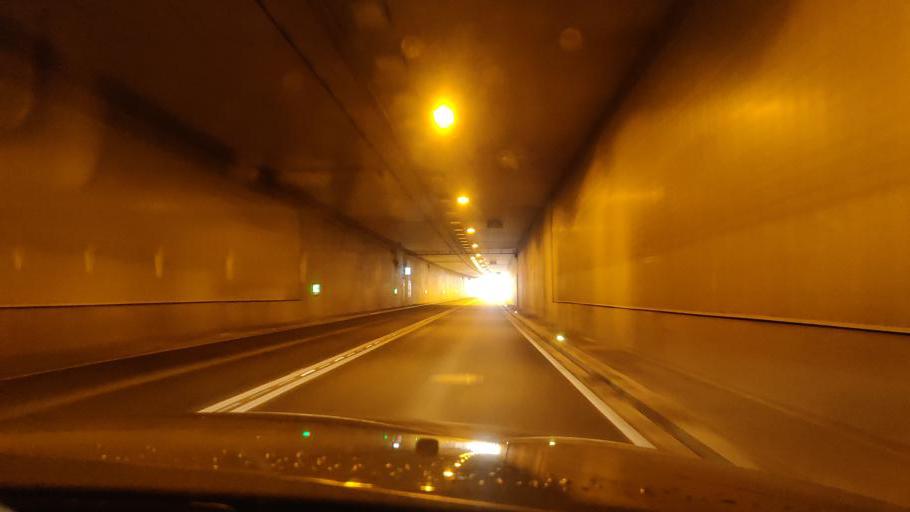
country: DE
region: Baden-Wuerttemberg
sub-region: Freiburg Region
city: Oberkirch
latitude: 48.5257
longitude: 8.0731
